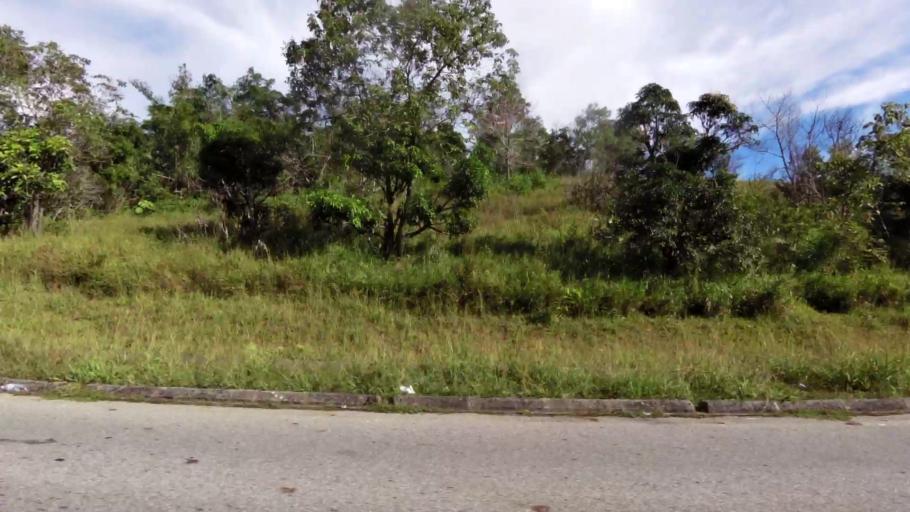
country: BN
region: Brunei and Muara
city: Bandar Seri Begawan
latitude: 4.9779
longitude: 114.9627
